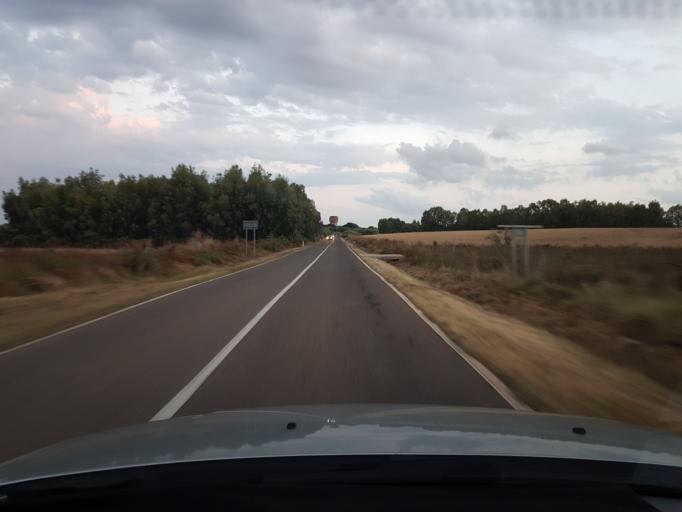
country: IT
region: Sardinia
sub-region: Provincia di Oristano
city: Tramatza
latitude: 40.0128
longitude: 8.6451
